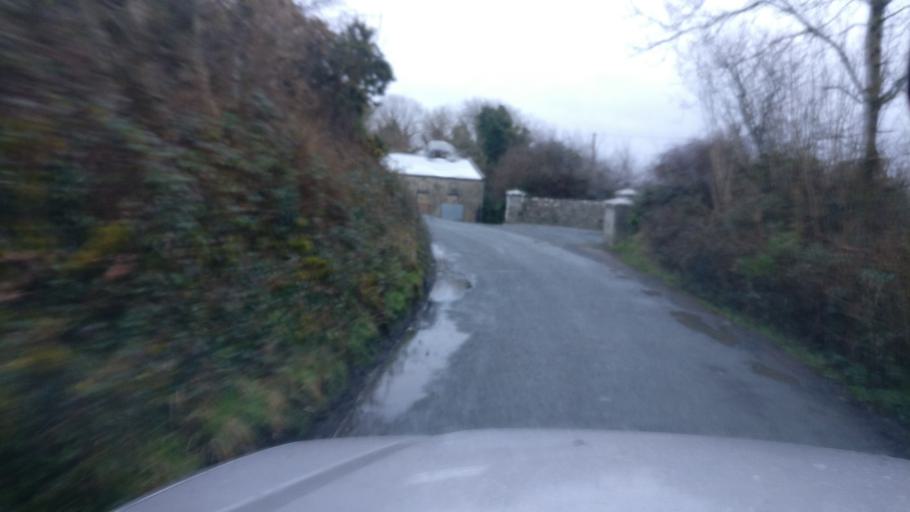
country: IE
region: Connaught
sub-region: County Galway
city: Ballinasloe
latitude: 53.2974
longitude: -8.2616
